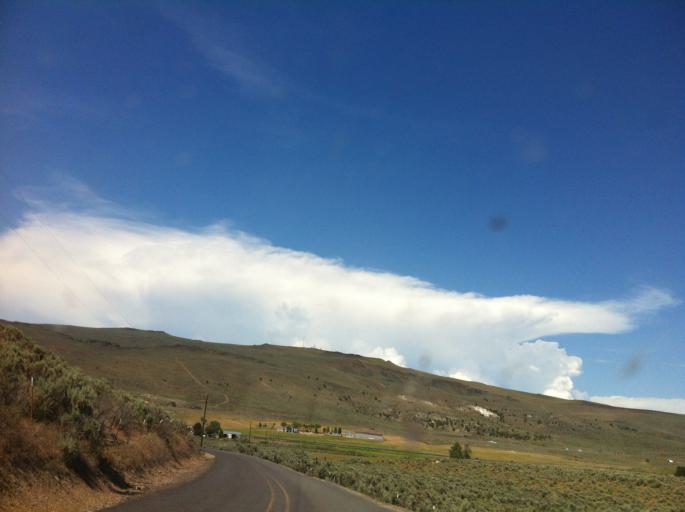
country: US
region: Oregon
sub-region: Baker County
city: Baker City
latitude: 44.7092
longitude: -117.7769
